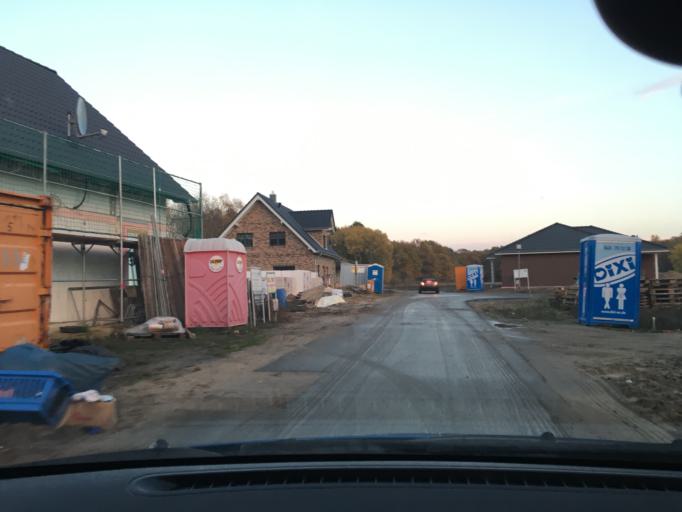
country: DE
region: Lower Saxony
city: Handorf
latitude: 53.3387
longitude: 10.3177
